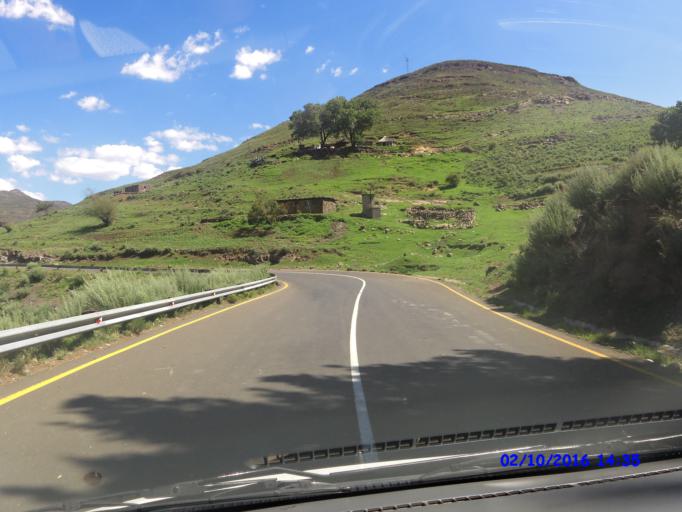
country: LS
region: Maseru
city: Nako
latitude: -29.4940
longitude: 28.0614
